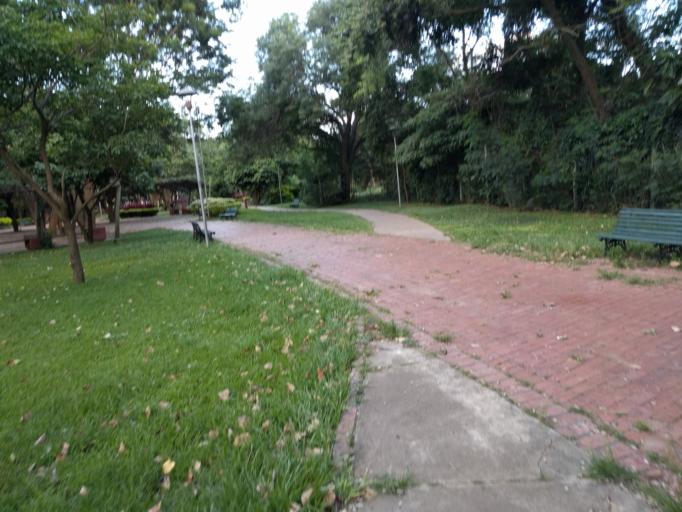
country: BO
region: Santa Cruz
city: Santa Cruz de la Sierra
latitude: -17.7822
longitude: -63.2194
